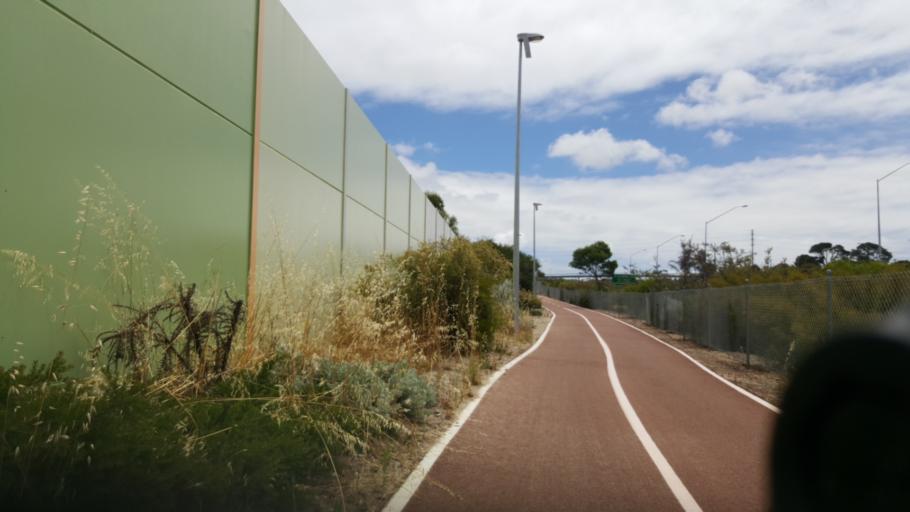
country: AU
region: Western Australia
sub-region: Bayswater
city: Embleton
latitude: -31.8684
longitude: 115.8922
